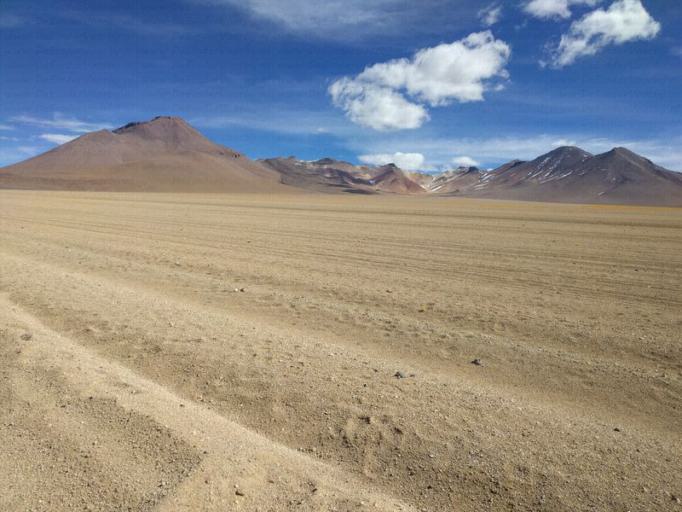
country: CL
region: Antofagasta
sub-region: Provincia de El Loa
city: San Pedro de Atacama
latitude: -22.6109
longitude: -67.6908
